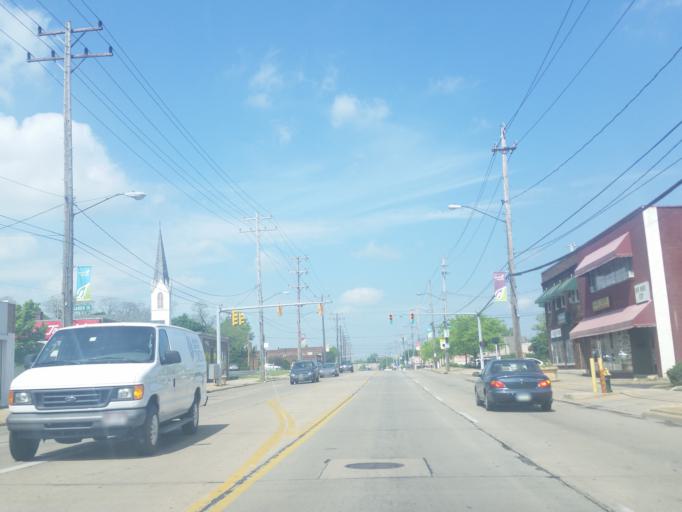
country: US
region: Ohio
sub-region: Cuyahoga County
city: South Euclid
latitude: 41.5201
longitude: -81.5199
